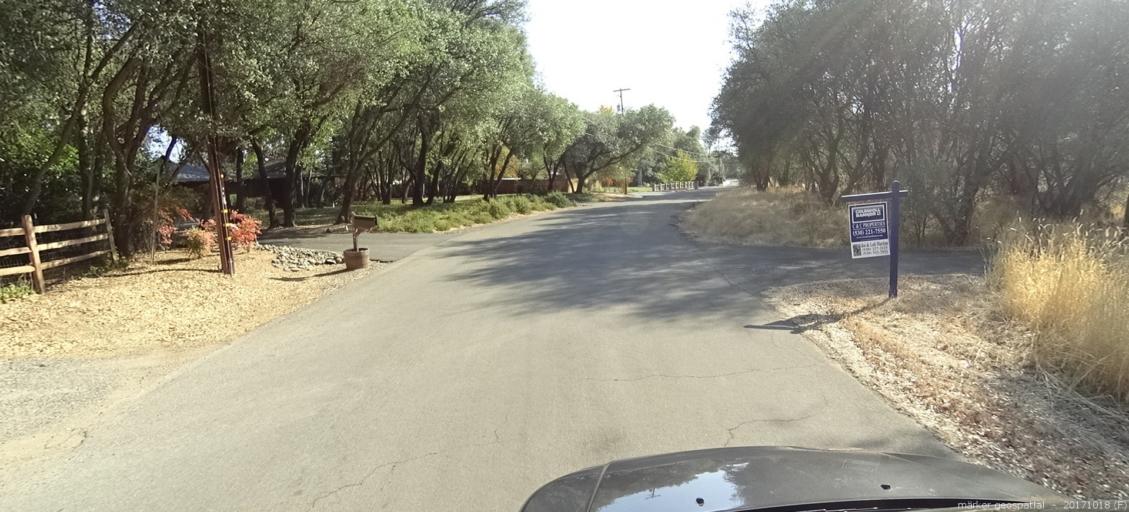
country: US
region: California
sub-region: Shasta County
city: Palo Cedro
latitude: 40.5744
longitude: -122.2288
